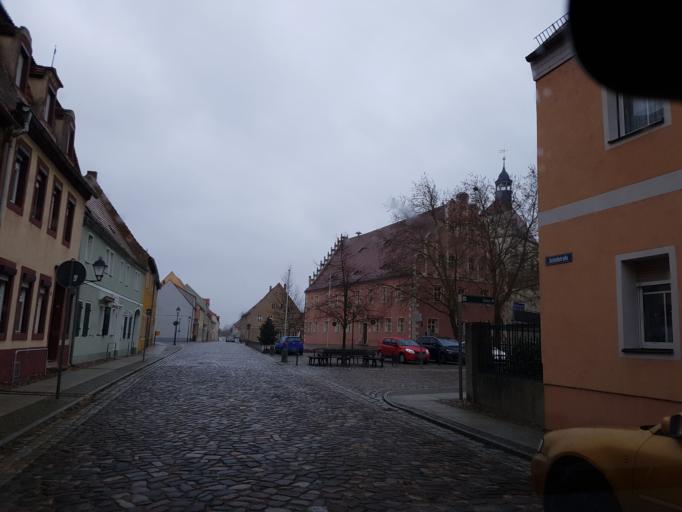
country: DE
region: Brandenburg
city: Muhlberg
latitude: 51.4329
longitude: 13.2137
